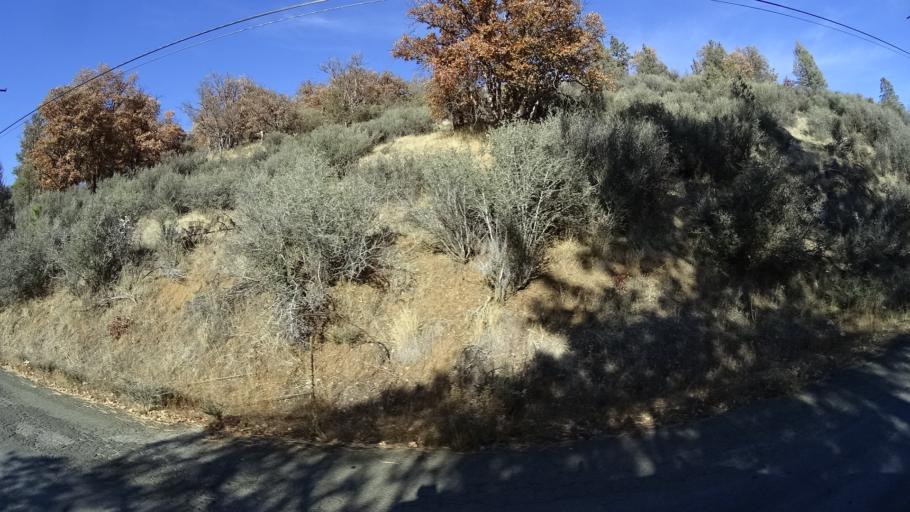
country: US
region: California
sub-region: Siskiyou County
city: Yreka
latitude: 41.7187
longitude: -122.6791
